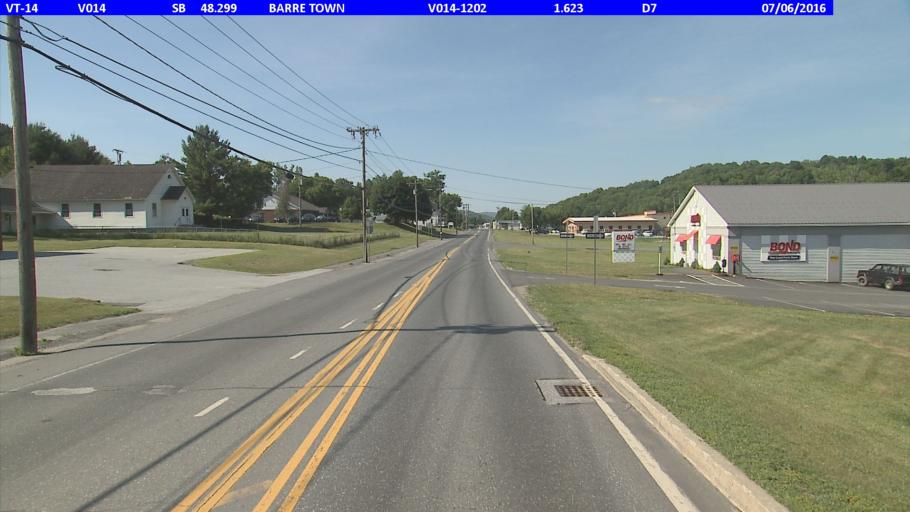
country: US
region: Vermont
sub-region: Washington County
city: South Barre
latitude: 44.1725
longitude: -72.5080
